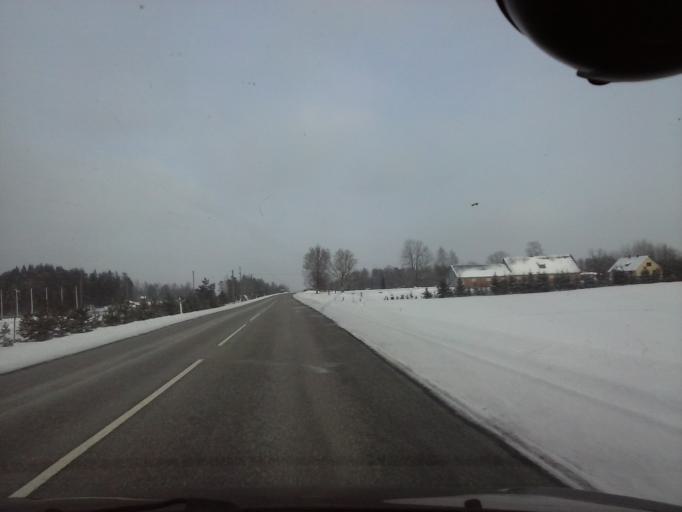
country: EE
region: Paernumaa
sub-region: Saarde vald
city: Kilingi-Nomme
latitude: 58.1661
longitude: 25.0180
